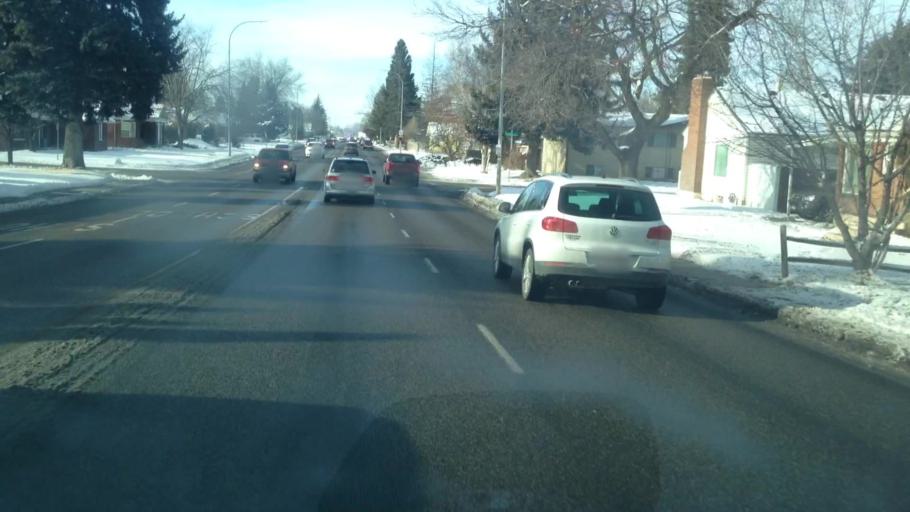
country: US
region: Idaho
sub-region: Bonneville County
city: Idaho Falls
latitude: 43.4826
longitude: -112.0354
